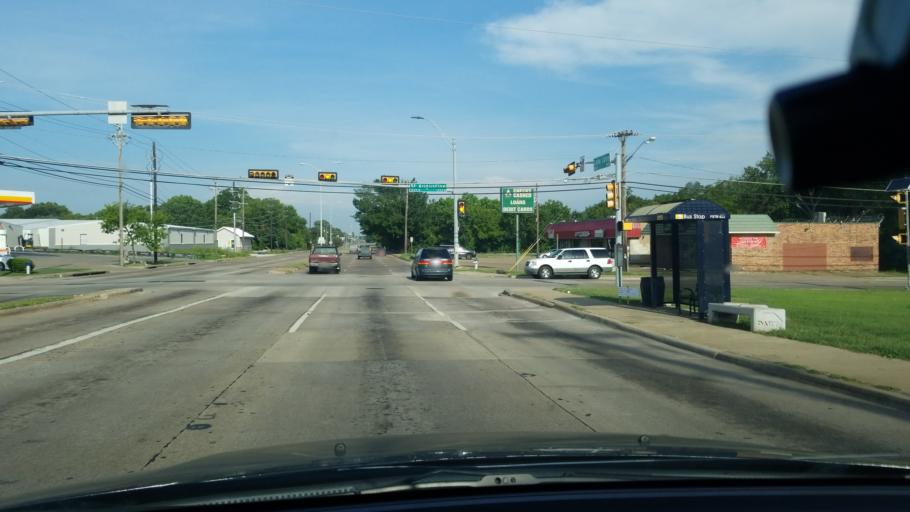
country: US
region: Texas
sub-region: Dallas County
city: Balch Springs
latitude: 32.7342
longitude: -96.6565
